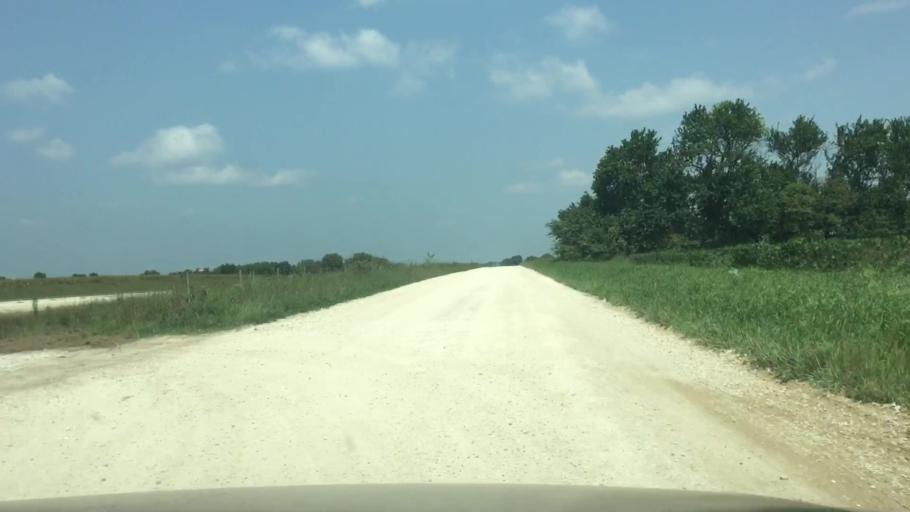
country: US
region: Kansas
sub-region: Allen County
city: Humboldt
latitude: 37.8379
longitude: -95.4094
